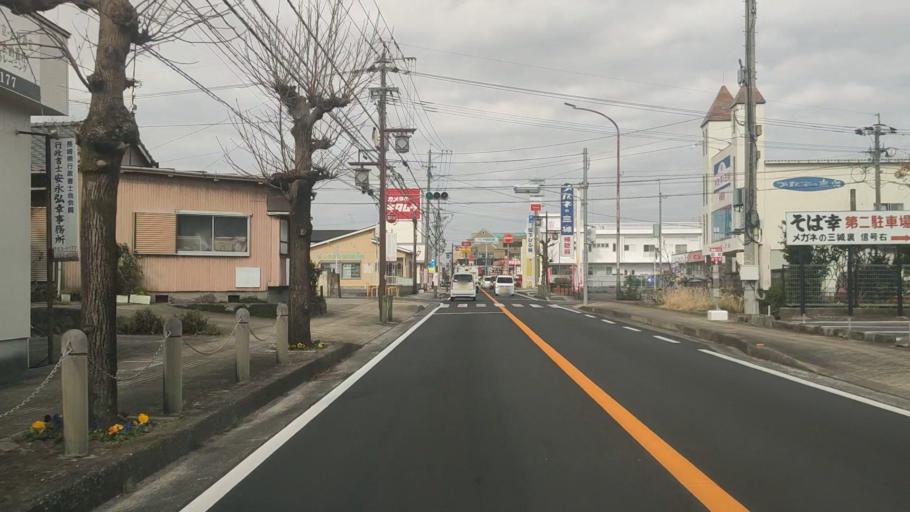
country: JP
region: Nagasaki
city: Shimabara
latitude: 32.7949
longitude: 130.3681
